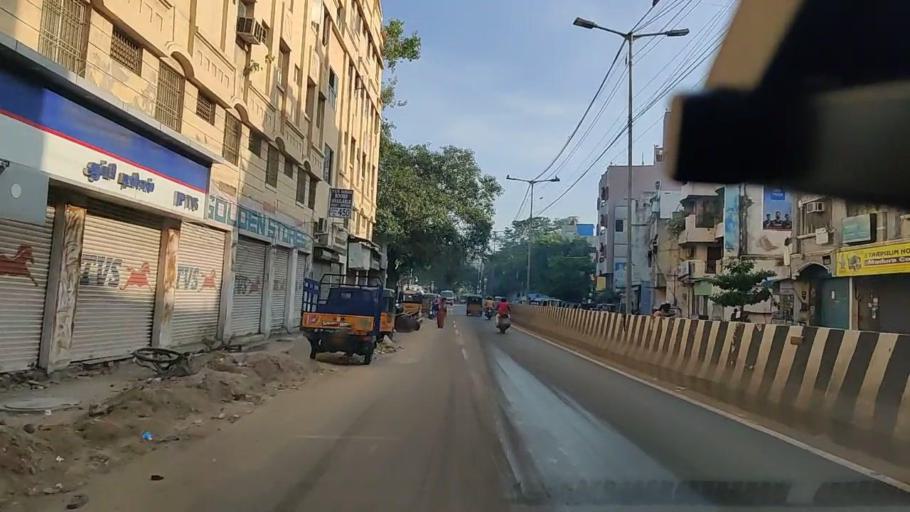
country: IN
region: Tamil Nadu
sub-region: Chennai
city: George Town
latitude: 13.0928
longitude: 80.2752
